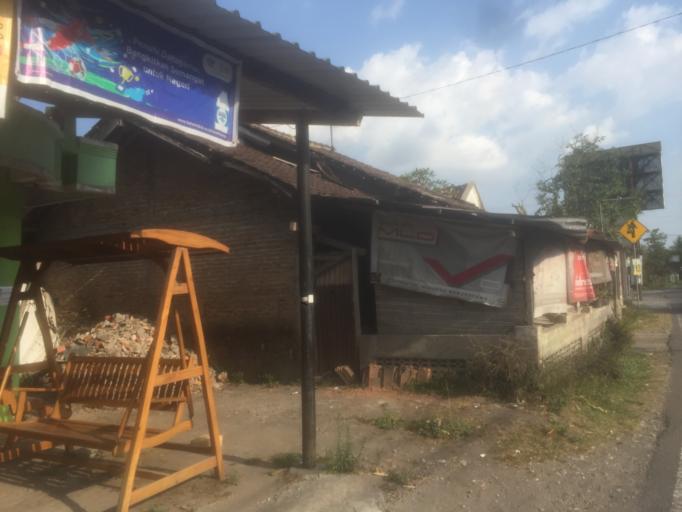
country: ID
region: Daerah Istimewa Yogyakarta
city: Sleman
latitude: -7.6462
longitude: 110.4243
